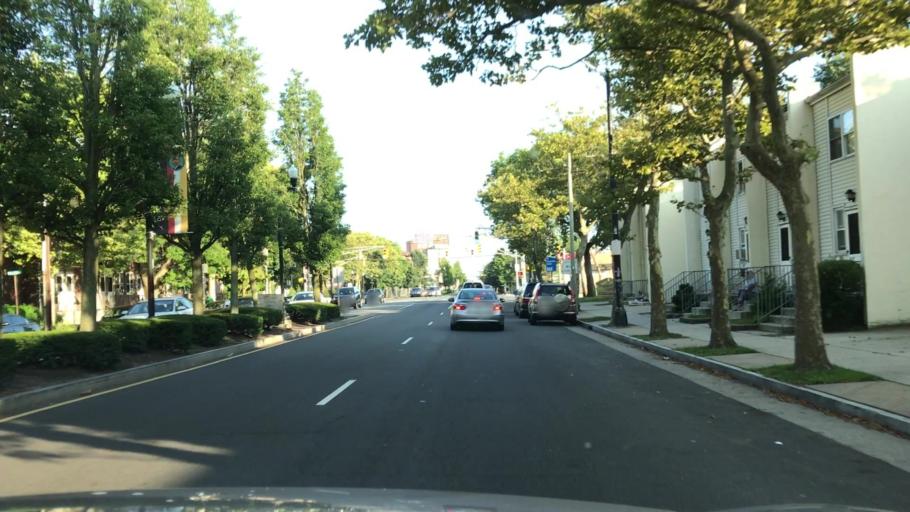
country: US
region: New Jersey
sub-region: Atlantic County
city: Atlantic City
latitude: 39.3643
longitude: -74.4345
